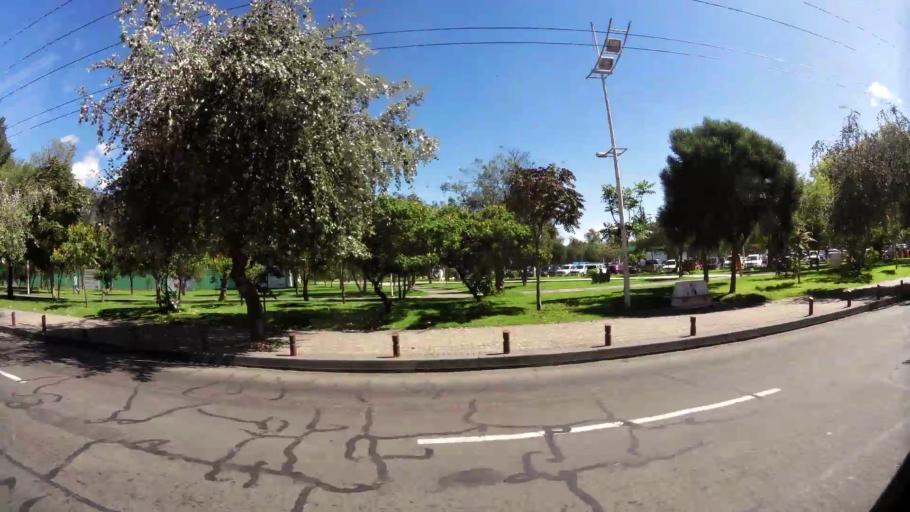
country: EC
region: Pichincha
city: Quito
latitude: -0.1901
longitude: -78.4846
